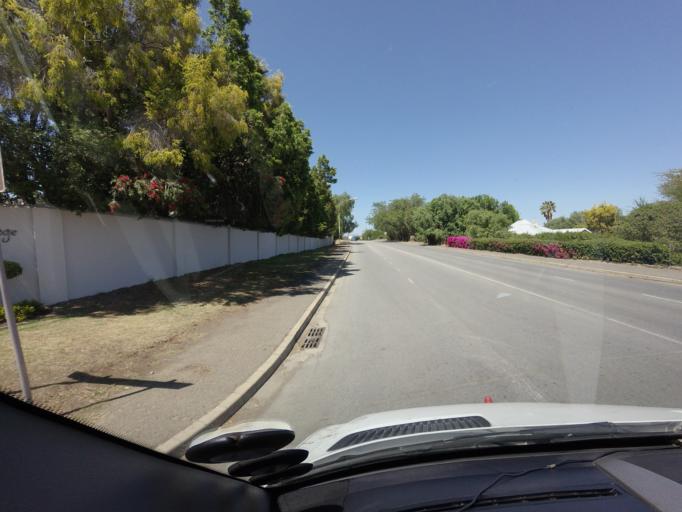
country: ZA
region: Western Cape
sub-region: Eden District Municipality
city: Oudtshoorn
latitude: -33.5758
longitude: 22.2061
